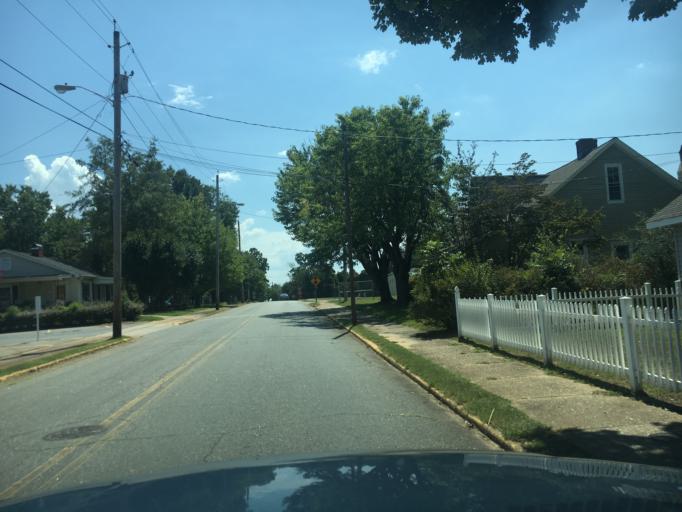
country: US
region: North Carolina
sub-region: Rutherford County
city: Forest City
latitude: 35.3321
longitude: -81.8636
